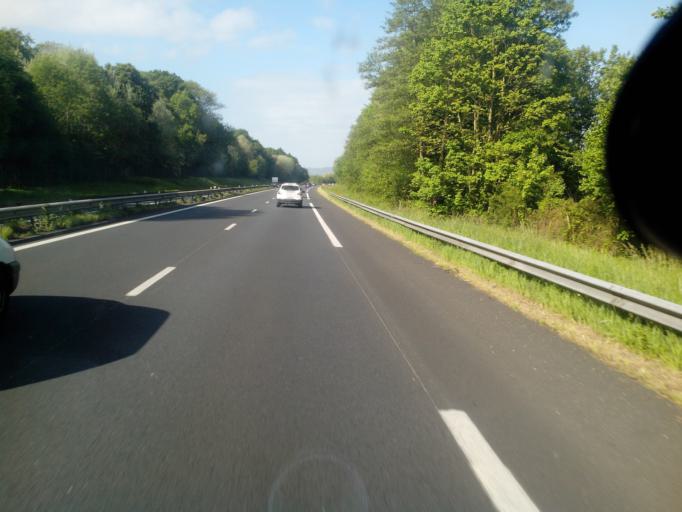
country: FR
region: Lower Normandy
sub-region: Departement du Calvados
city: Troarn
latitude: 49.1942
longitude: -0.1856
